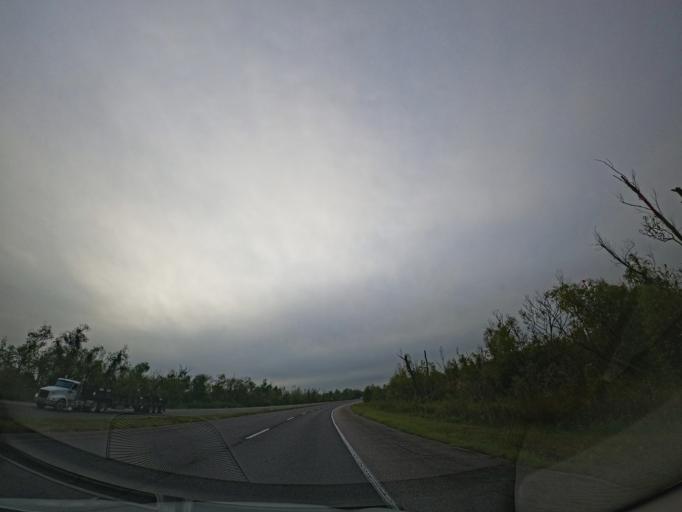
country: US
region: Louisiana
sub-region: Terrebonne Parish
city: Houma
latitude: 29.6360
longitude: -90.6643
